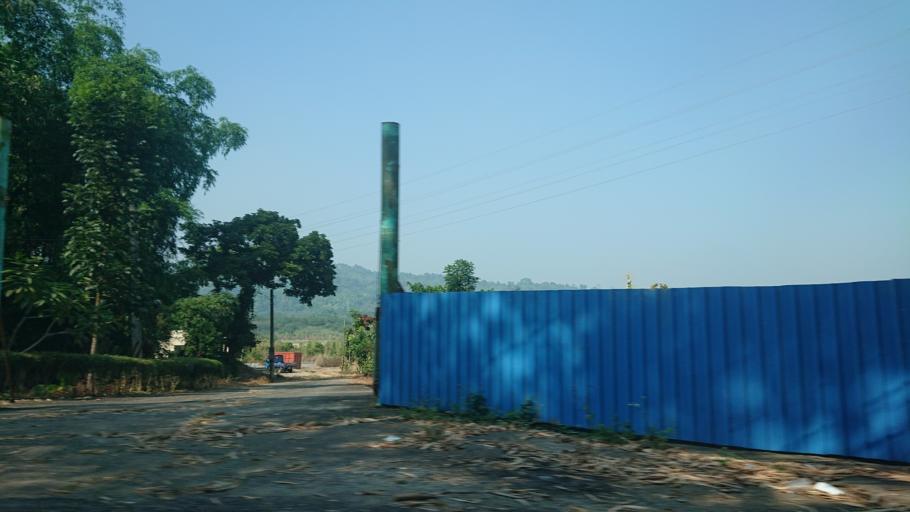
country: TW
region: Taiwan
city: Lugu
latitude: 23.7094
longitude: 120.6653
